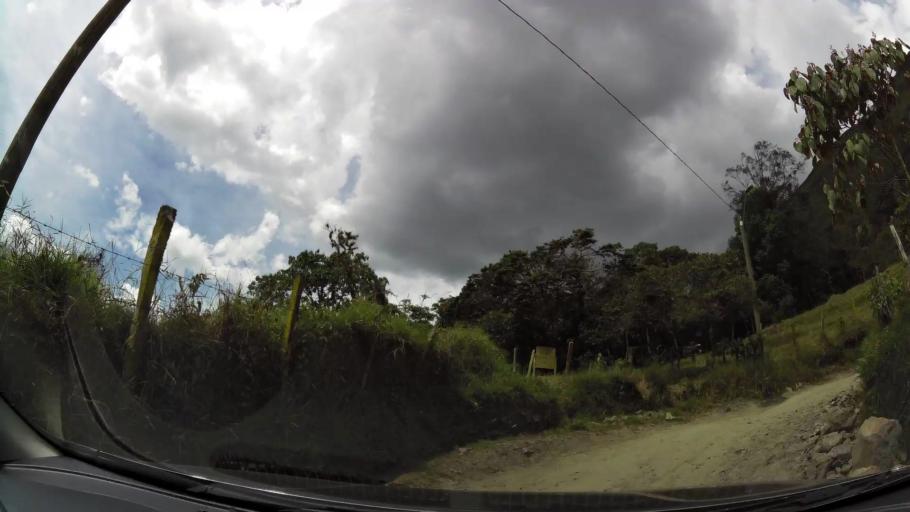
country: CO
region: Antioquia
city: Municipio de Copacabana
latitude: 6.3227
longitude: -75.4930
